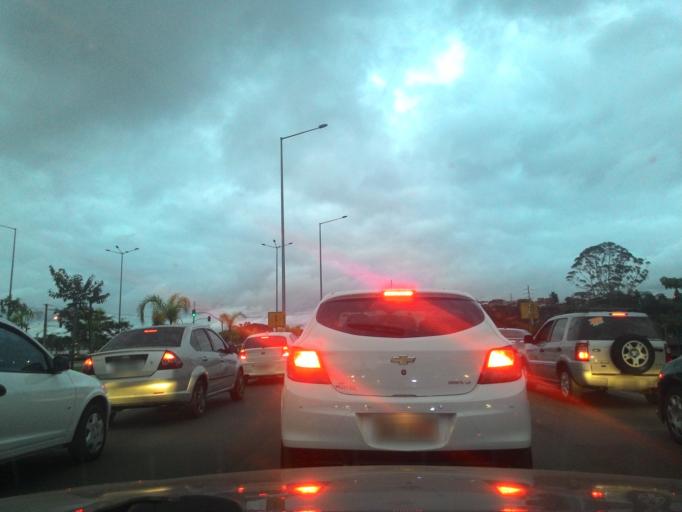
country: BR
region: Parana
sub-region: Curitiba
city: Curitiba
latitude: -25.4603
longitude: -49.2501
